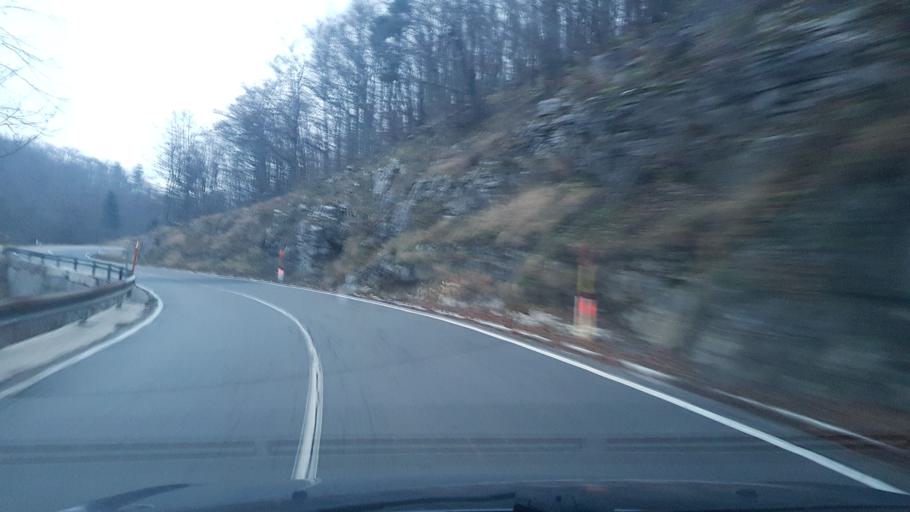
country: SI
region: Idrija
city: Idrija
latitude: 45.9117
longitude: 14.0279
